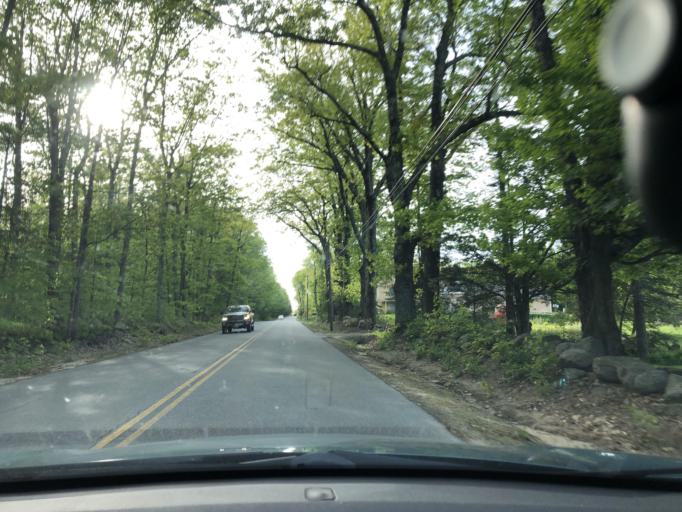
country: US
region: New Hampshire
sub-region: Merrimack County
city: New London
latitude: 43.4109
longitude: -71.9643
